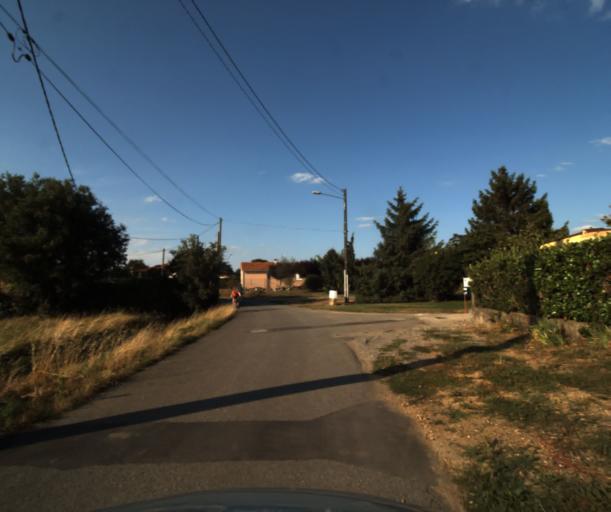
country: FR
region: Midi-Pyrenees
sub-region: Departement de la Haute-Garonne
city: Saint-Lys
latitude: 43.5031
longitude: 1.1865
